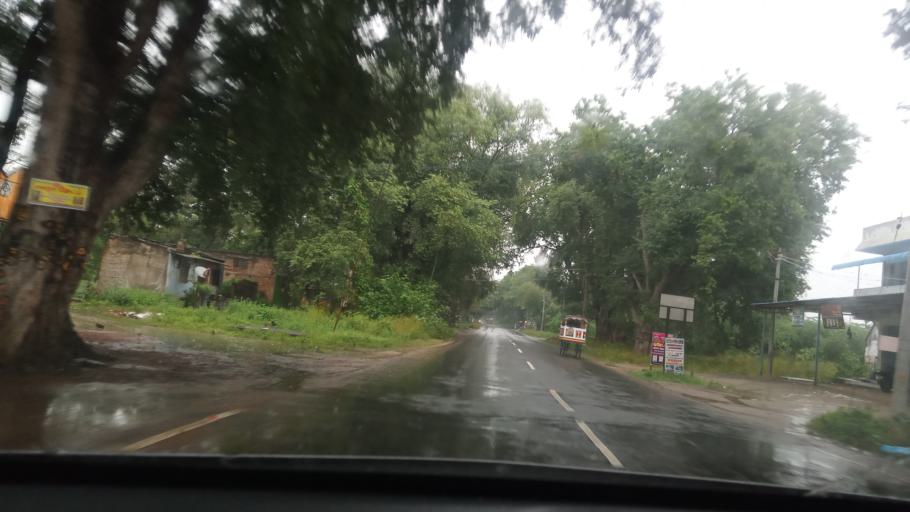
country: IN
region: Tamil Nadu
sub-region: Vellore
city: Kalavai
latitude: 12.8058
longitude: 79.4142
